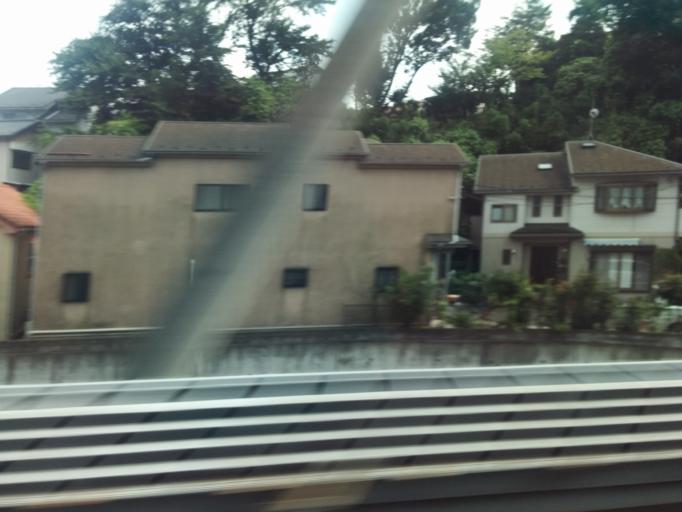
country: JP
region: Kanagawa
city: Yokohama
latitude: 35.4799
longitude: 139.5694
